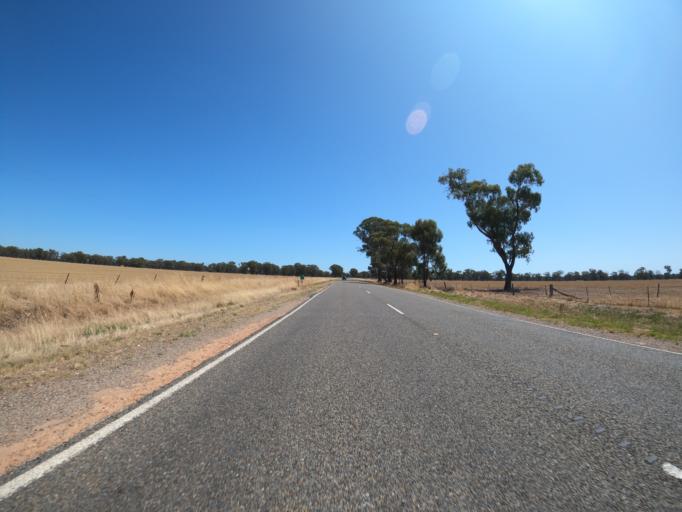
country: AU
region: New South Wales
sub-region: Corowa Shire
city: Corowa
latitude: -36.0783
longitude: 146.3427
